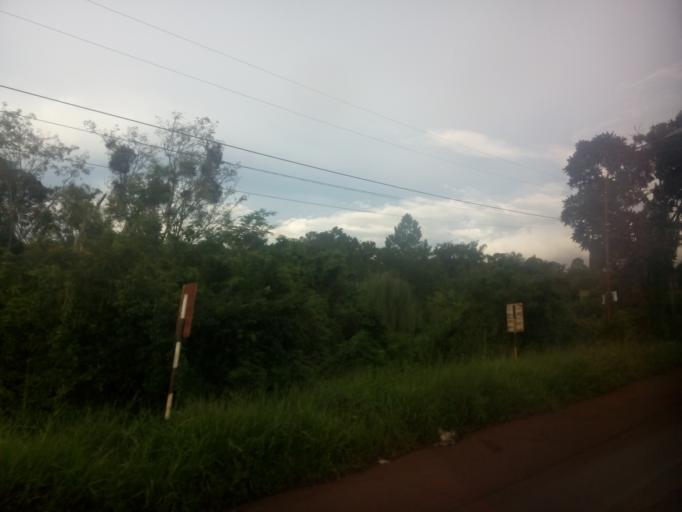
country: AR
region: Misiones
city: Guarani
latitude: -27.4912
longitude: -55.1538
